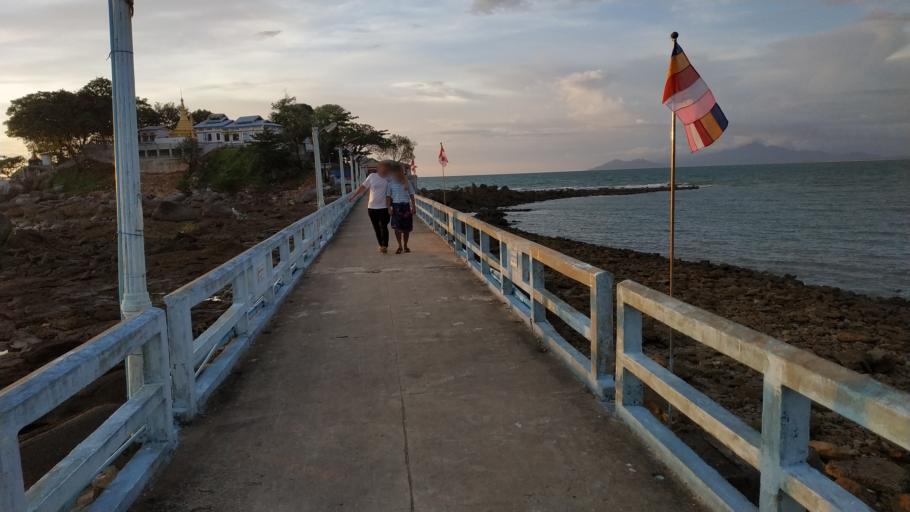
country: MM
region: Tanintharyi
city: Dawei
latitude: 14.0863
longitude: 98.0710
